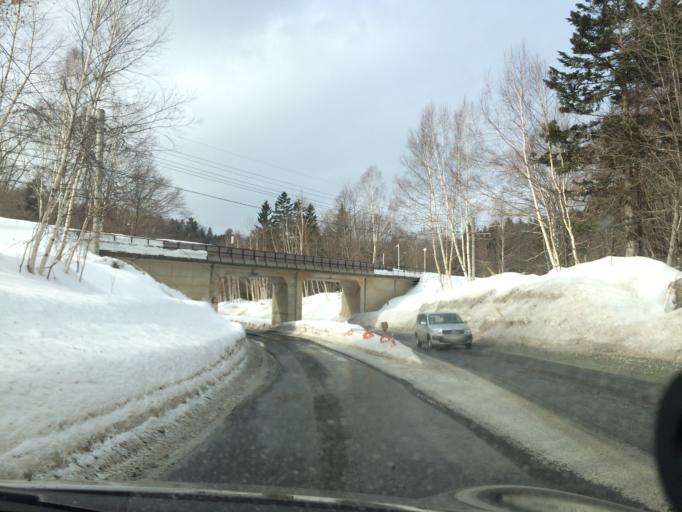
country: JP
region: Hokkaido
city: Shimo-furano
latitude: 43.0802
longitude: 142.6772
